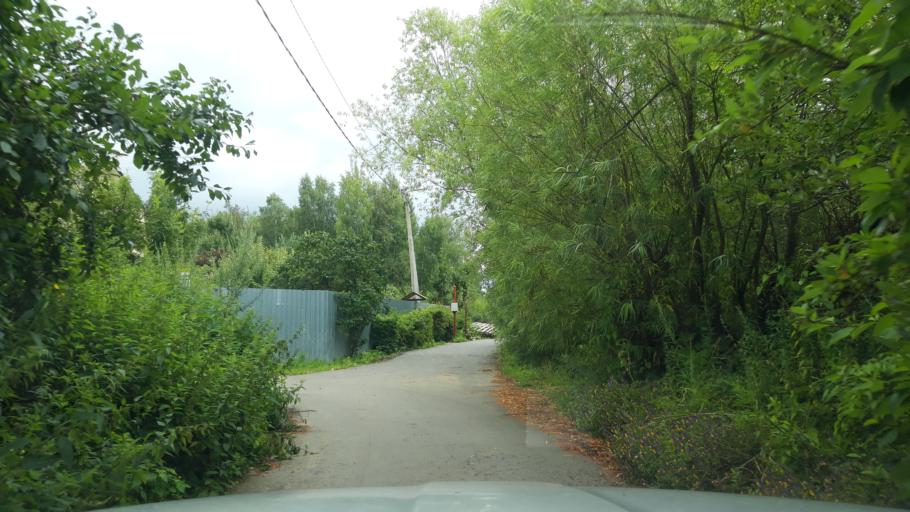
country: RU
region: Moskovskaya
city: Povarovo
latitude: 56.0675
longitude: 37.0737
